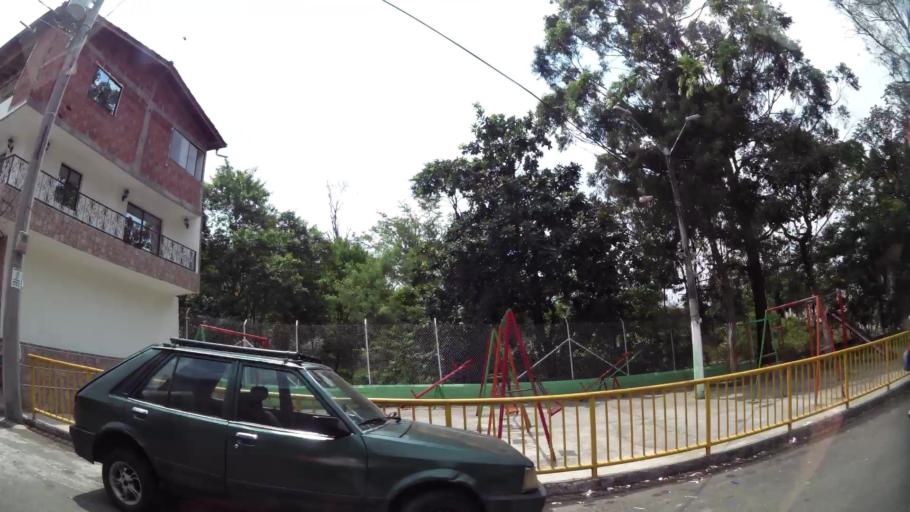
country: CO
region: Antioquia
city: Medellin
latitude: 6.2618
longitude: -75.5490
